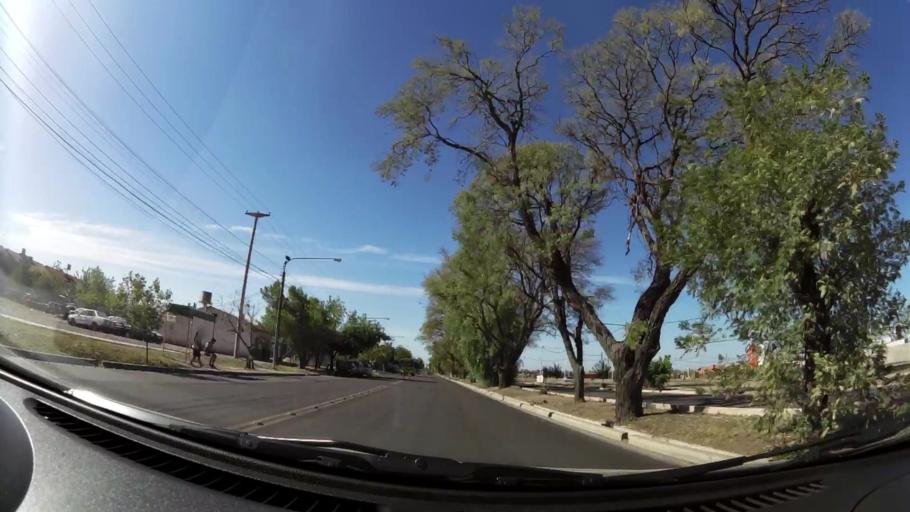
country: AR
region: Mendoza
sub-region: Departamento de Godoy Cruz
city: Godoy Cruz
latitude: -32.9417
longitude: -68.8040
